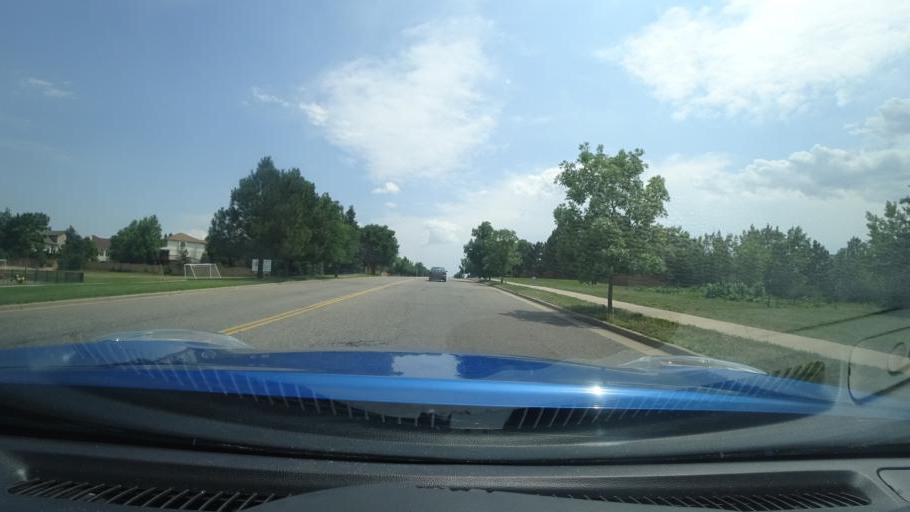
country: US
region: Colorado
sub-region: Adams County
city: Aurora
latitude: 39.6736
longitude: -104.7788
